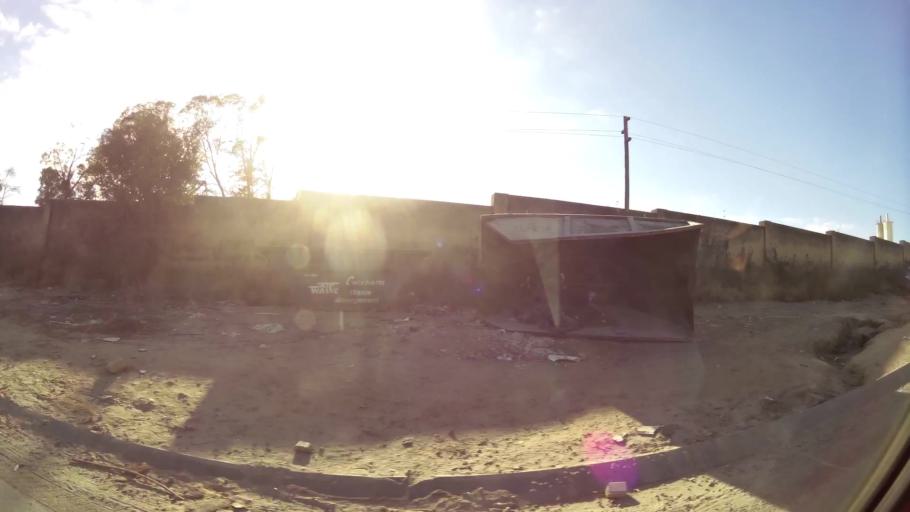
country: ZA
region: Gauteng
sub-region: City of Johannesburg Metropolitan Municipality
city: Modderfontein
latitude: -26.0454
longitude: 28.1717
